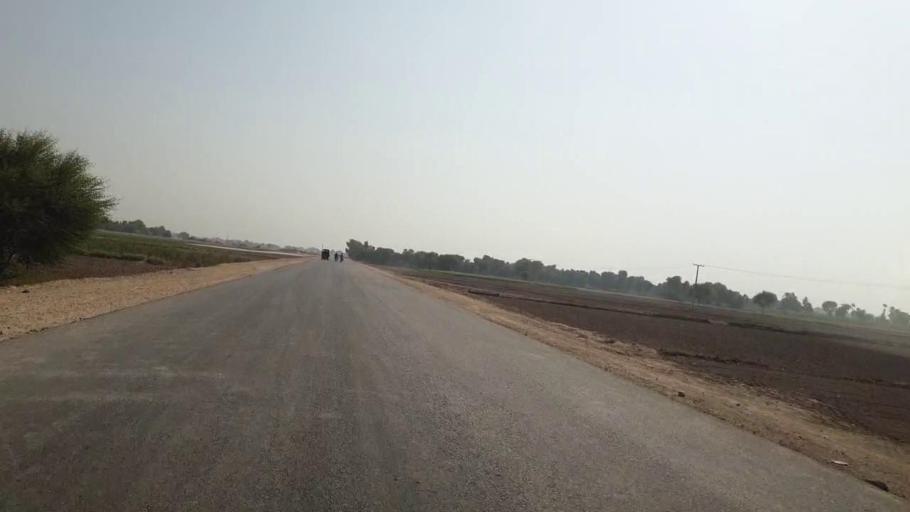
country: PK
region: Sindh
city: Dadu
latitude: 26.6526
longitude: 67.7763
